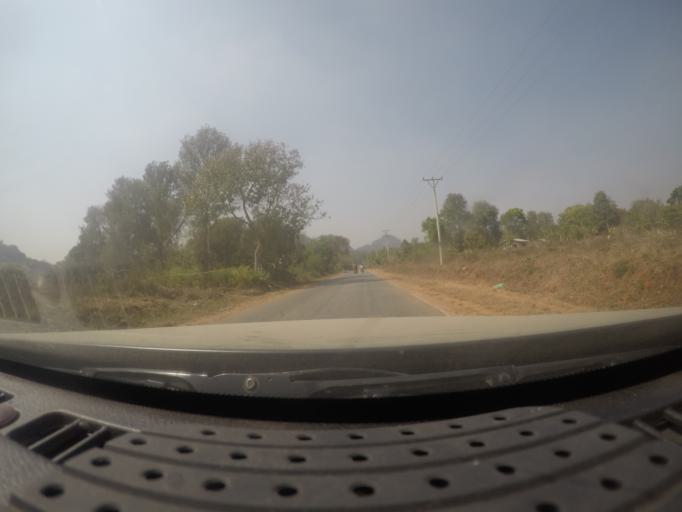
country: MM
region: Mandalay
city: Kyaukse
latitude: 21.1180
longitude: 96.4646
